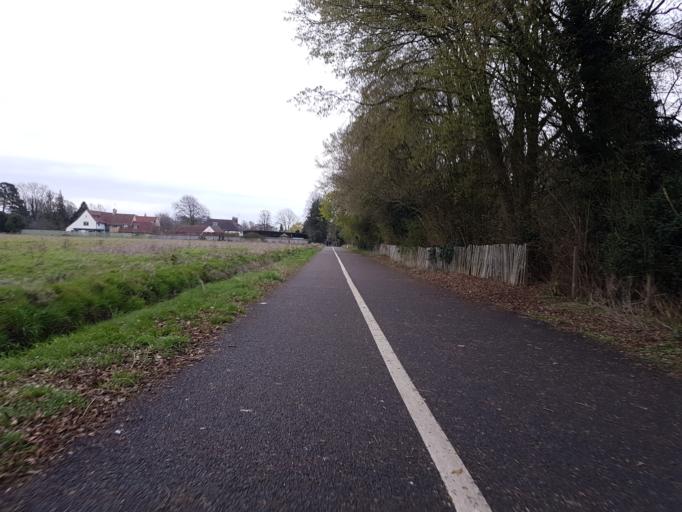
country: GB
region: England
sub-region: Cambridgeshire
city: Girton
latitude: 52.2171
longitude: 0.0959
